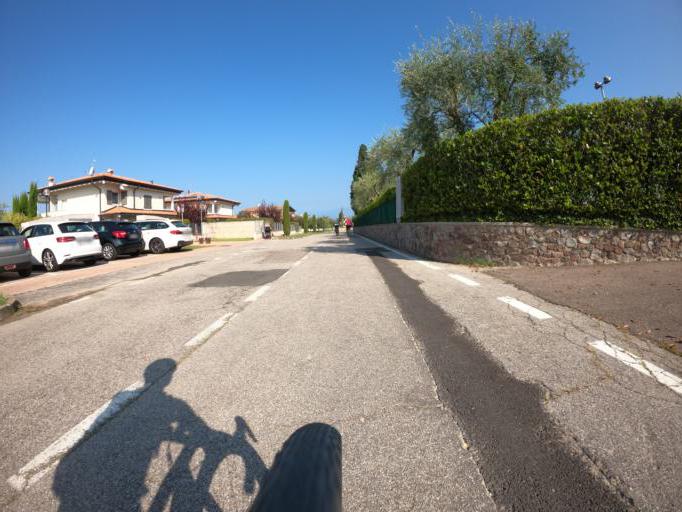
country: IT
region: Veneto
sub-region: Provincia di Verona
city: Lazise
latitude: 45.5109
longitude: 10.7403
